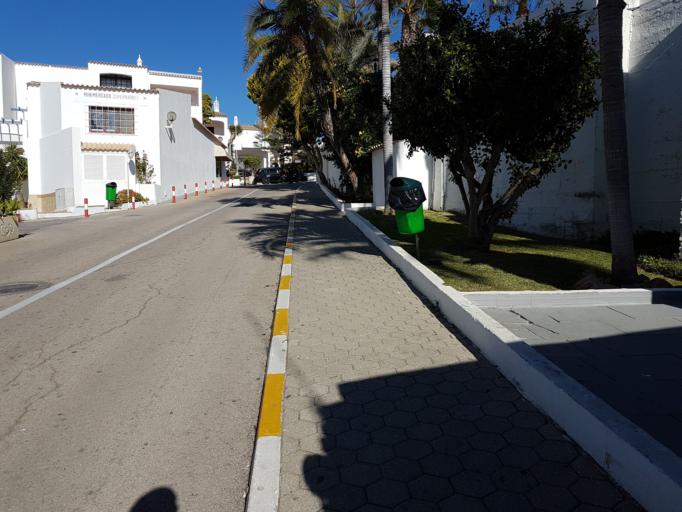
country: PT
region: Faro
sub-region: Albufeira
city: Albufeira
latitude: 37.0854
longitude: -8.2369
